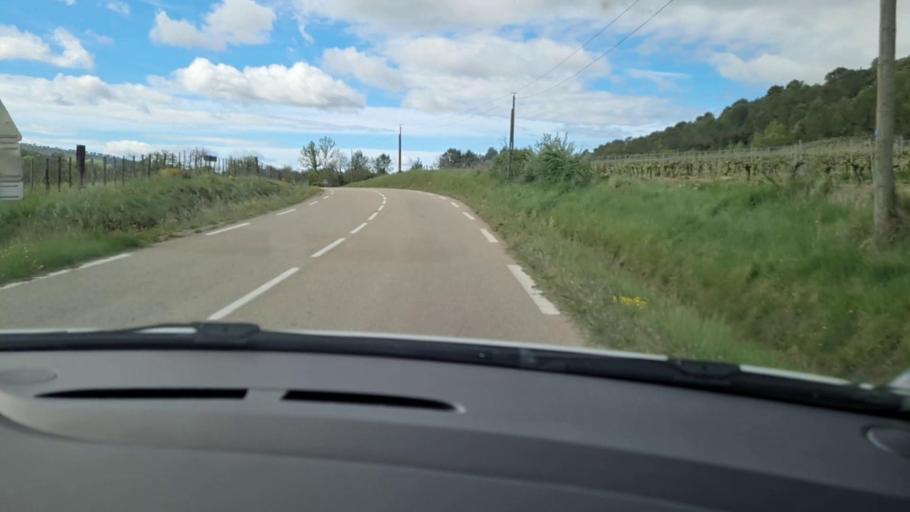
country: FR
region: Languedoc-Roussillon
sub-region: Departement du Gard
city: Quissac
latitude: 43.8688
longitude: 4.0155
